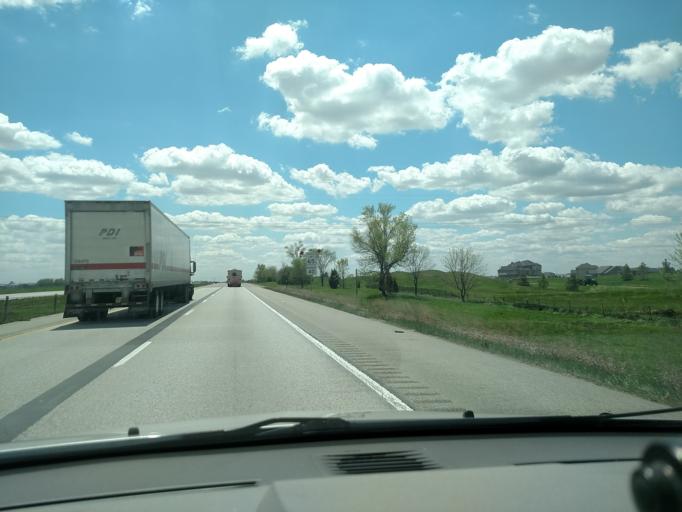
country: US
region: Iowa
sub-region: Polk County
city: Ankeny
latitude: 41.7733
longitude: -93.5708
